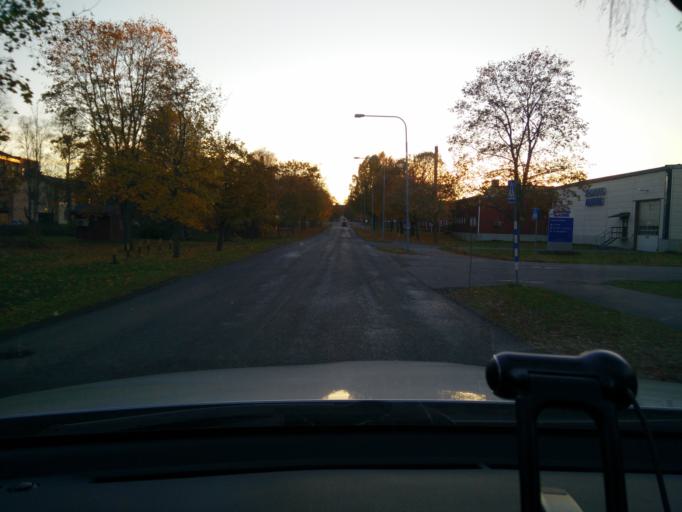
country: SE
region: Vaesternorrland
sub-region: Sundsvalls Kommun
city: Matfors
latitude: 62.3496
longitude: 17.0345
